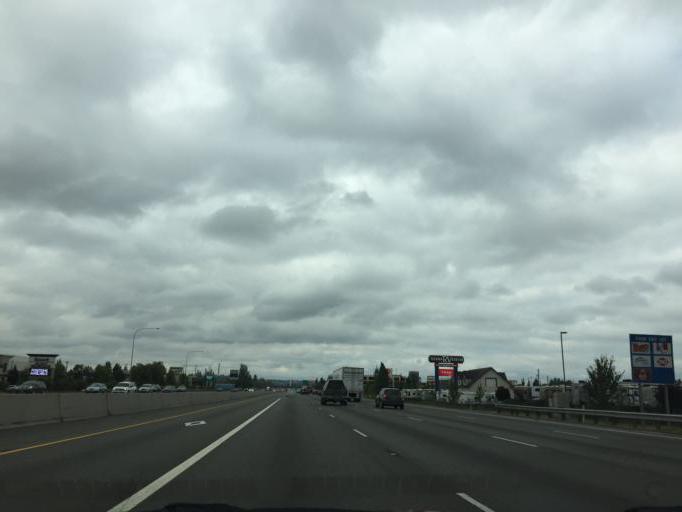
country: US
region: Washington
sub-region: Pierce County
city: Fife
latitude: 47.2413
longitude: -122.3440
